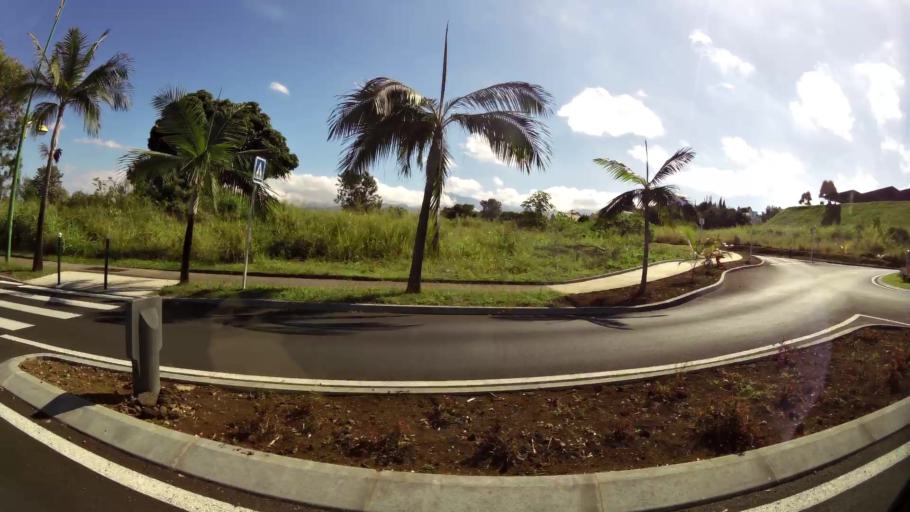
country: RE
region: Reunion
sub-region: Reunion
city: Le Tampon
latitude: -21.2742
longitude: 55.5063
